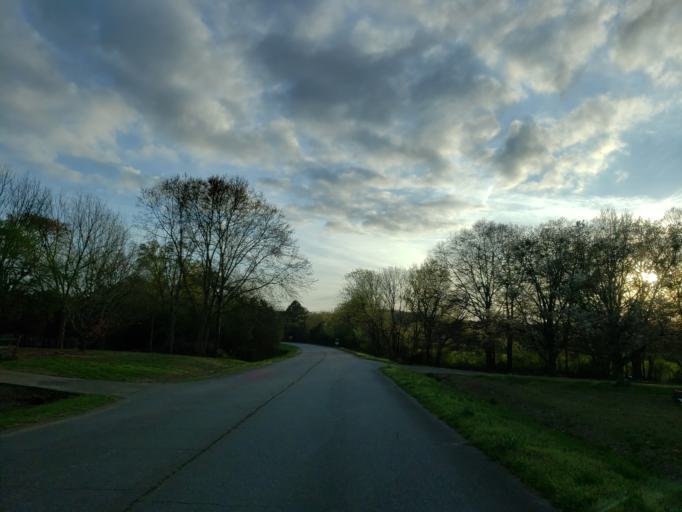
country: US
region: Georgia
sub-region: Bartow County
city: Euharlee
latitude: 34.0835
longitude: -84.9818
